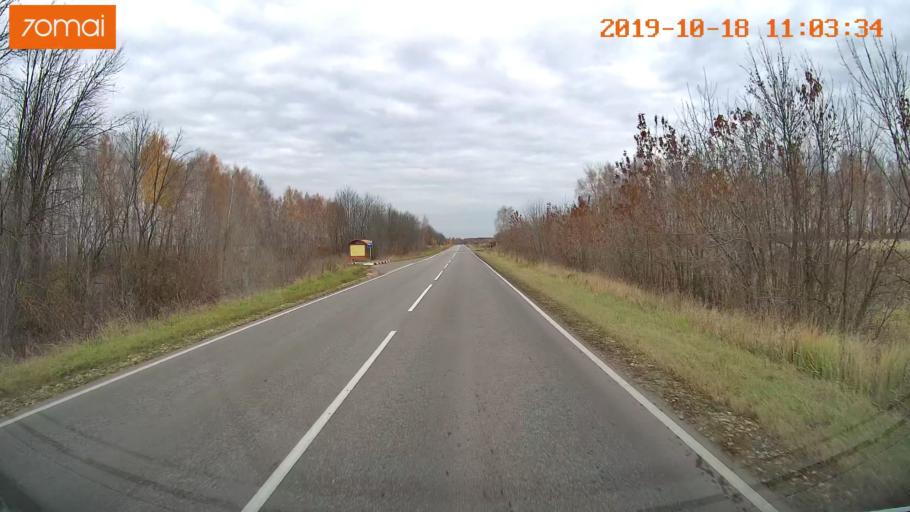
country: RU
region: Tula
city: Yepifan'
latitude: 53.8816
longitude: 38.5489
